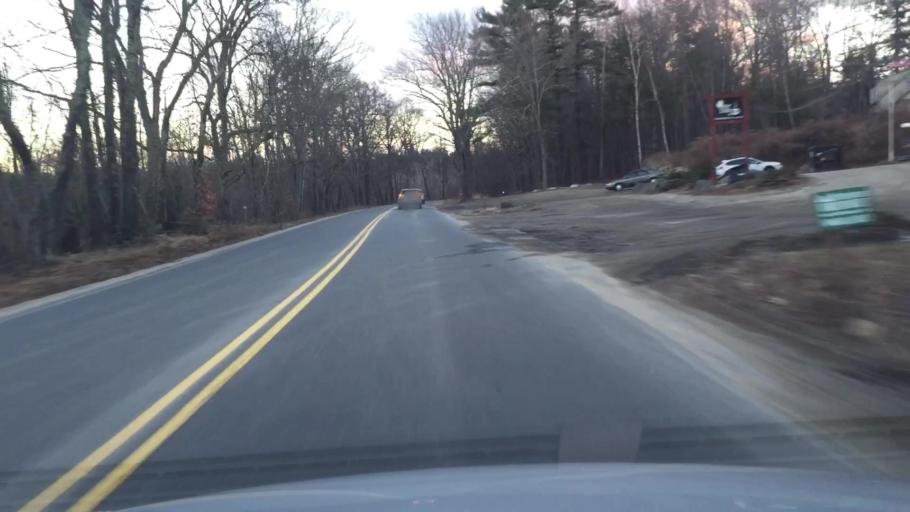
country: US
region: Massachusetts
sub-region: Worcester County
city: Sterling
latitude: 42.4306
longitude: -71.8112
